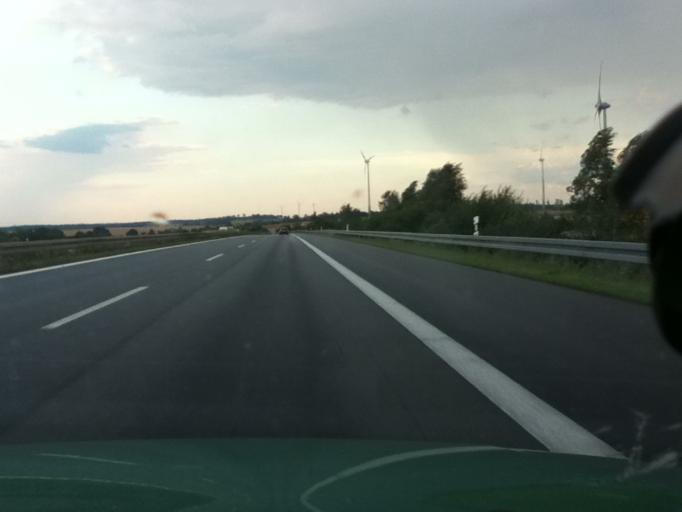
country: DE
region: Saxony
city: Wachau
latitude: 51.1655
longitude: 13.9219
